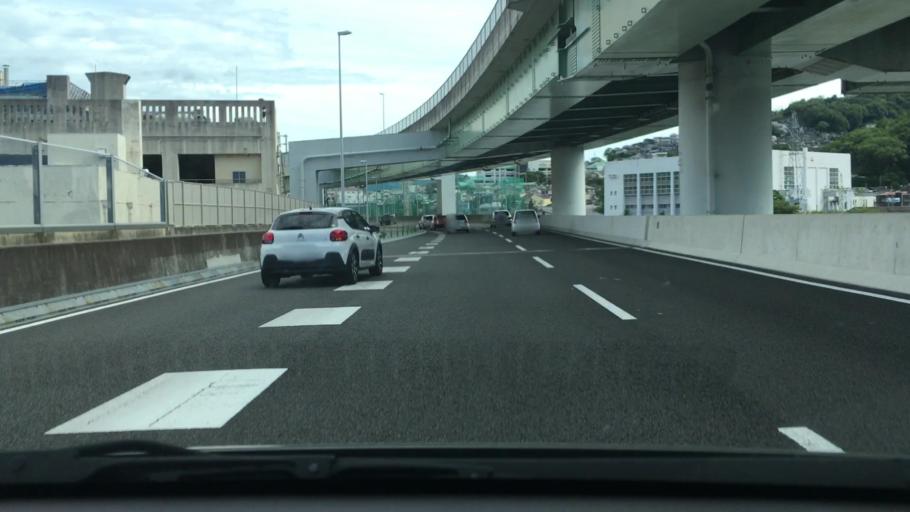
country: JP
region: Nagasaki
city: Nagasaki-shi
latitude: 32.7620
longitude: 129.8618
